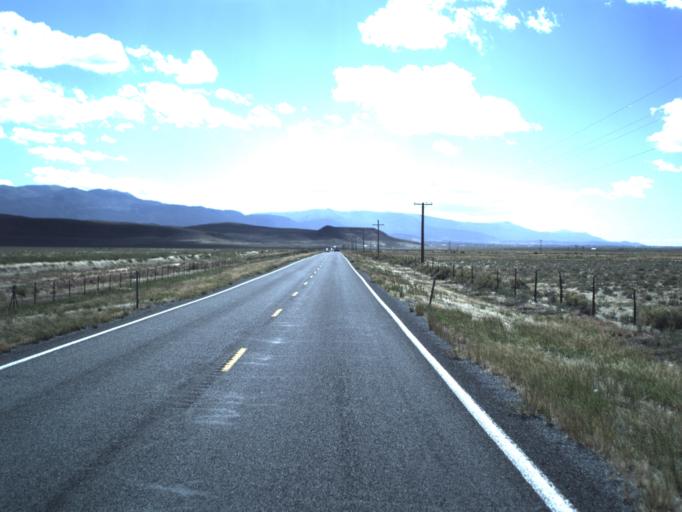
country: US
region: Utah
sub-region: Iron County
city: Enoch
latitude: 37.8839
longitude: -113.0316
